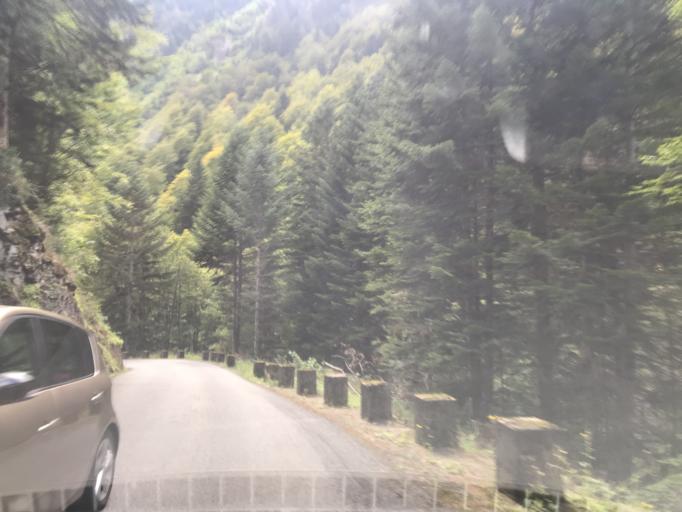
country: FR
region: Midi-Pyrenees
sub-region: Departement des Hautes-Pyrenees
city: Saint-Lary-Soulan
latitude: 42.8103
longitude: 0.2214
